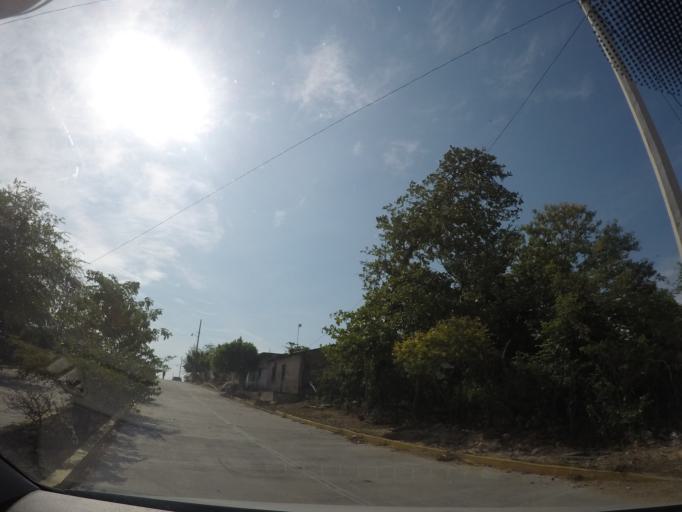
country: MX
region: Oaxaca
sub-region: Salina Cruz
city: Salina Cruz
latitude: 16.2195
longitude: -95.1293
